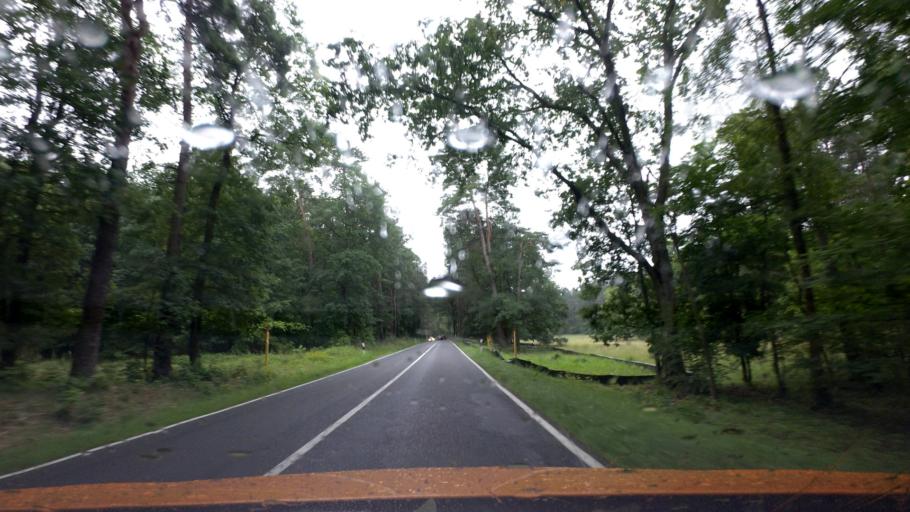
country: DE
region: Brandenburg
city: Strausberg
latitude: 52.5999
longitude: 13.8869
